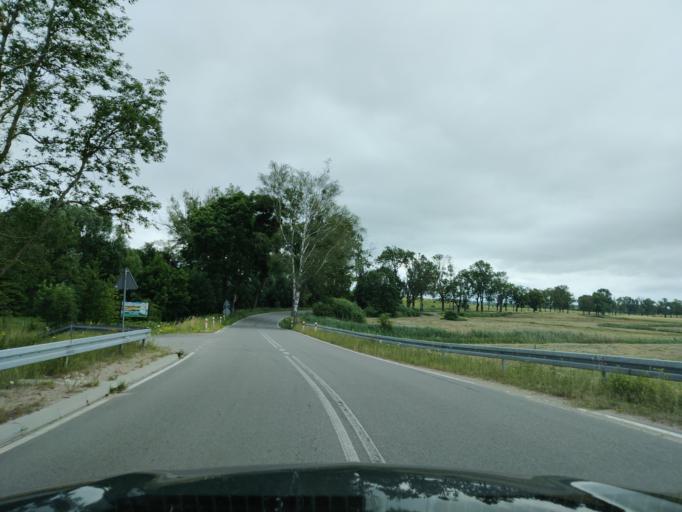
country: PL
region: Warmian-Masurian Voivodeship
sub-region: Powiat mragowski
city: Mikolajki
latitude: 53.8750
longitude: 21.5928
